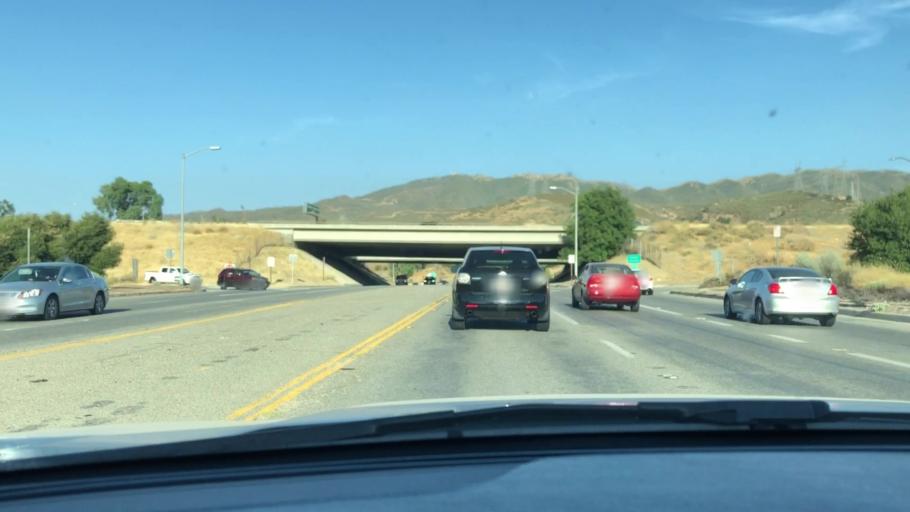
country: US
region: California
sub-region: Los Angeles County
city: Santa Clarita
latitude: 34.3655
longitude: -118.5050
